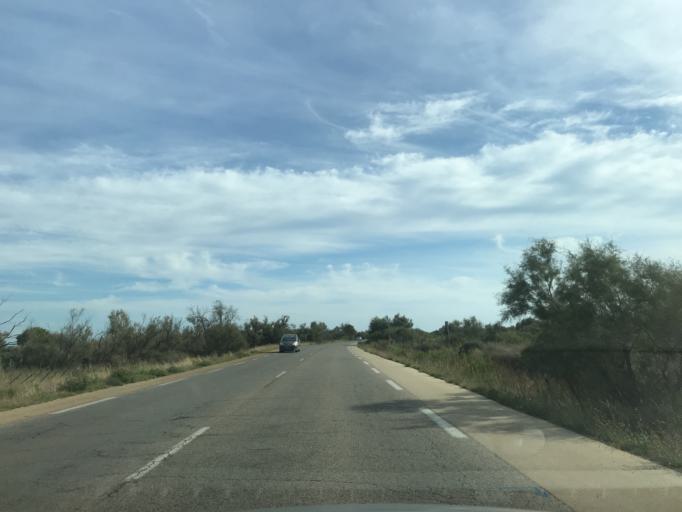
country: FR
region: Provence-Alpes-Cote d'Azur
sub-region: Departement des Bouches-du-Rhone
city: Saintes-Maries-de-la-Mer
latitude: 43.4940
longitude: 4.4033
